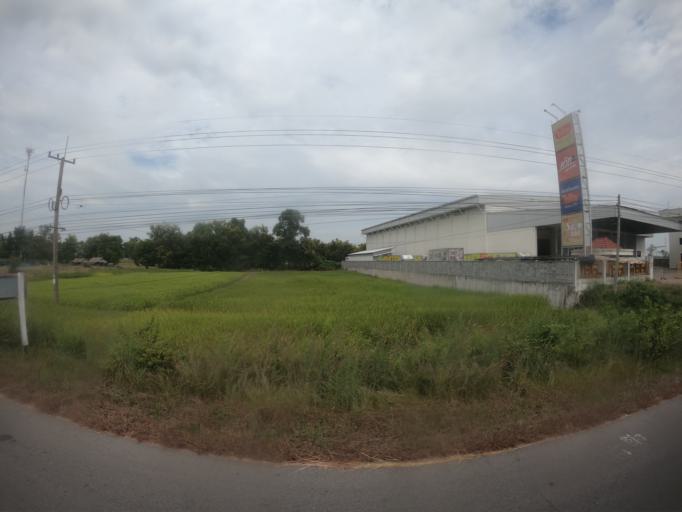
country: TH
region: Roi Et
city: Changhan
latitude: 16.0956
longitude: 103.5381
